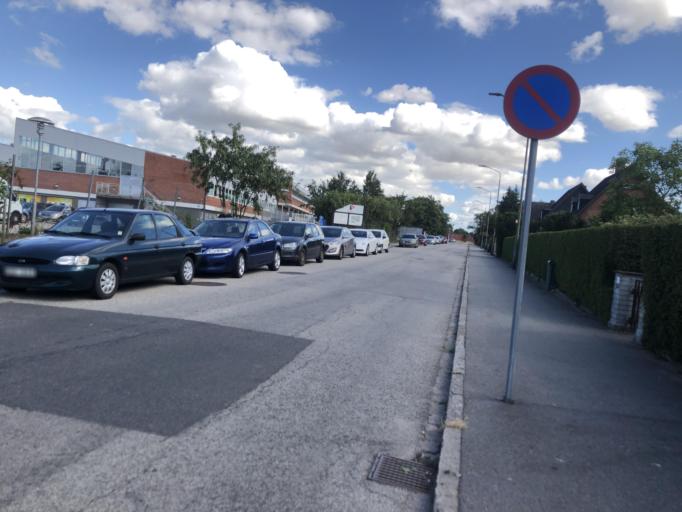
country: SE
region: Skane
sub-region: Malmo
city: Malmoe
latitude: 55.5757
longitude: 13.0265
